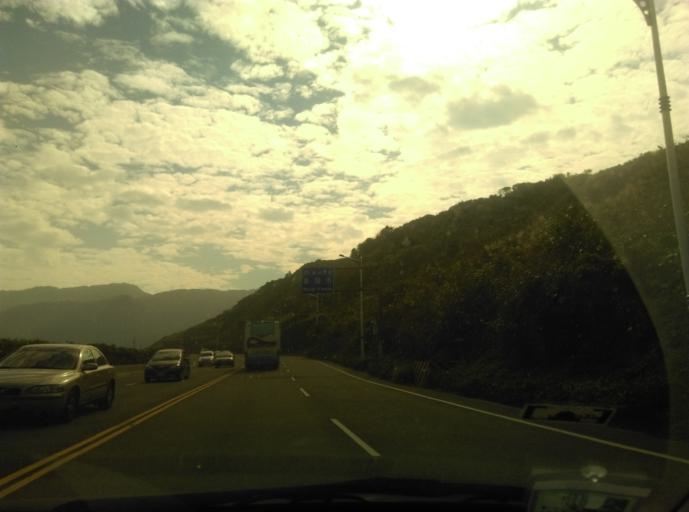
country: TW
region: Taiwan
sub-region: Keelung
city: Keelung
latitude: 25.1733
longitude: 121.7083
